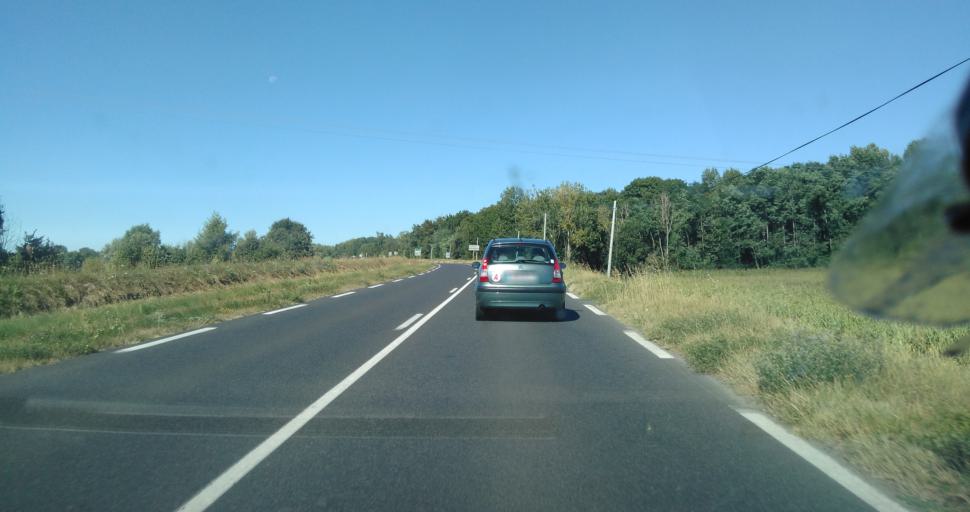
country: FR
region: Centre
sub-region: Departement d'Indre-et-Loire
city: Noizay
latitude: 47.4039
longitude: 0.9038
